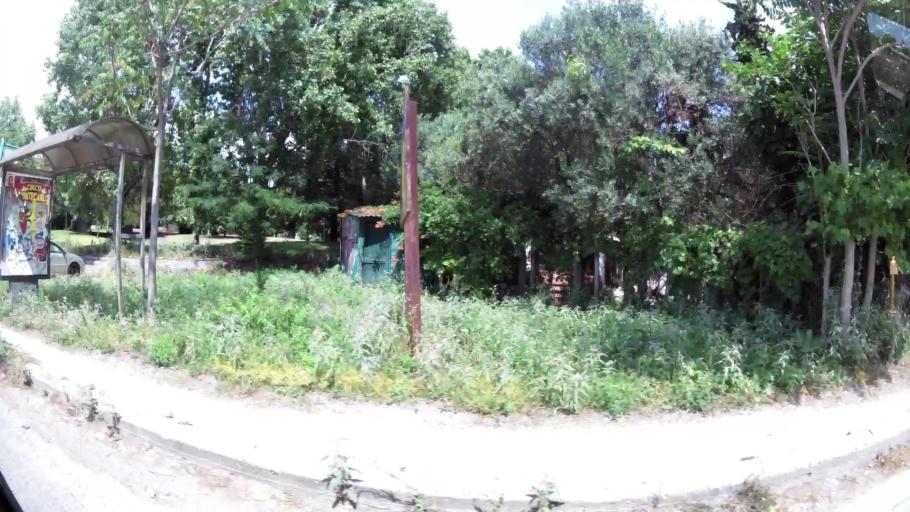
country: GR
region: Central Macedonia
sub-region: Nomos Thessalonikis
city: Pylaia
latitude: 40.5936
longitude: 22.9722
